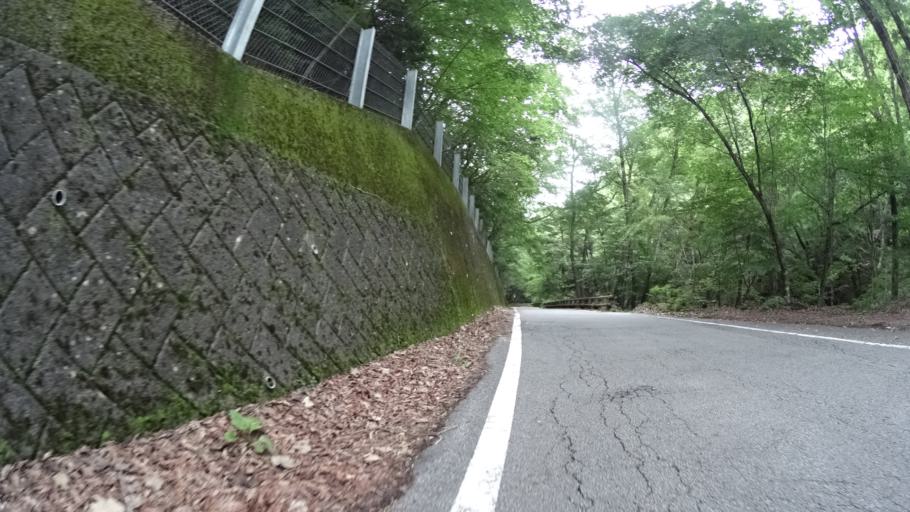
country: JP
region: Yamanashi
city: Nirasaki
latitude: 35.8628
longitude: 138.5539
